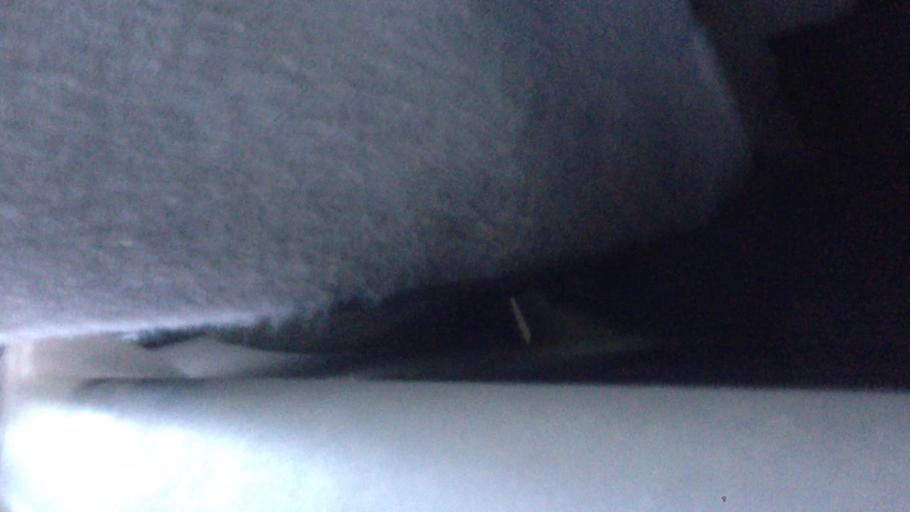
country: US
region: New York
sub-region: Dutchess County
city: Tivoli
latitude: 42.0643
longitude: -73.8404
